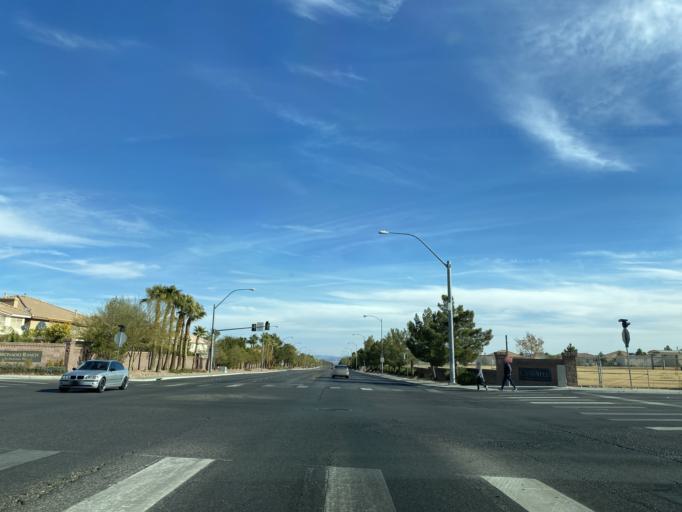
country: US
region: Nevada
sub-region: Clark County
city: Enterprise
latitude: 36.0489
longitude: -115.2345
